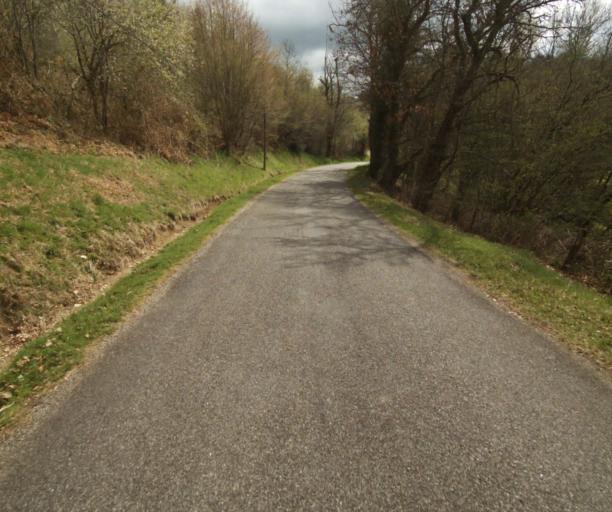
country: FR
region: Limousin
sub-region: Departement de la Correze
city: Laguenne
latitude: 45.2402
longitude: 1.8901
